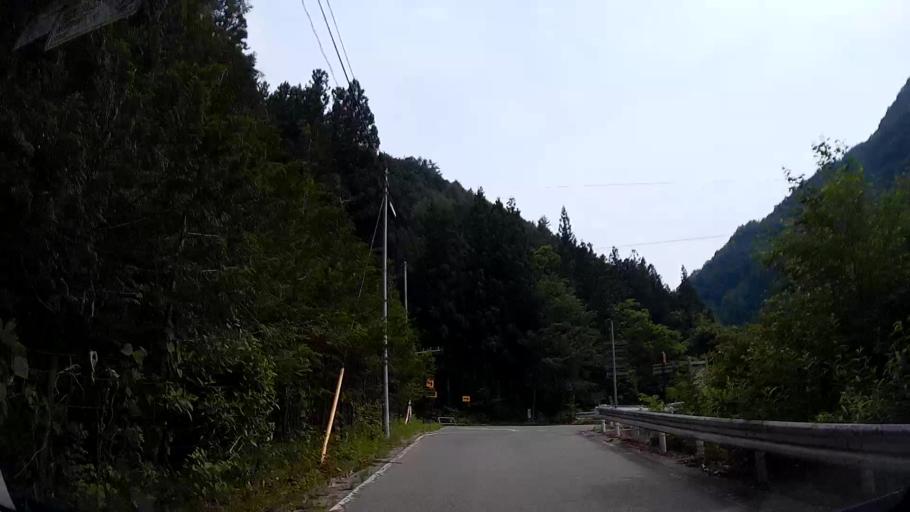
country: JP
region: Nagano
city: Iida
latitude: 35.4438
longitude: 137.9920
